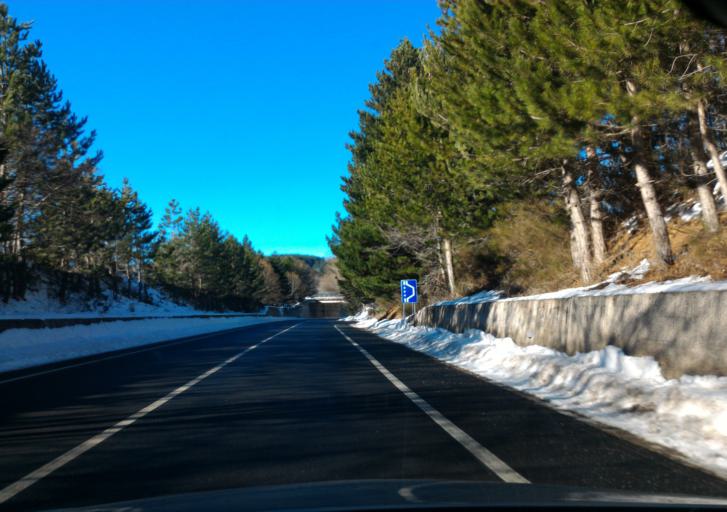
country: IT
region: Calabria
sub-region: Provincia di Cosenza
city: Celico
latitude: 39.3286
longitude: 16.4863
